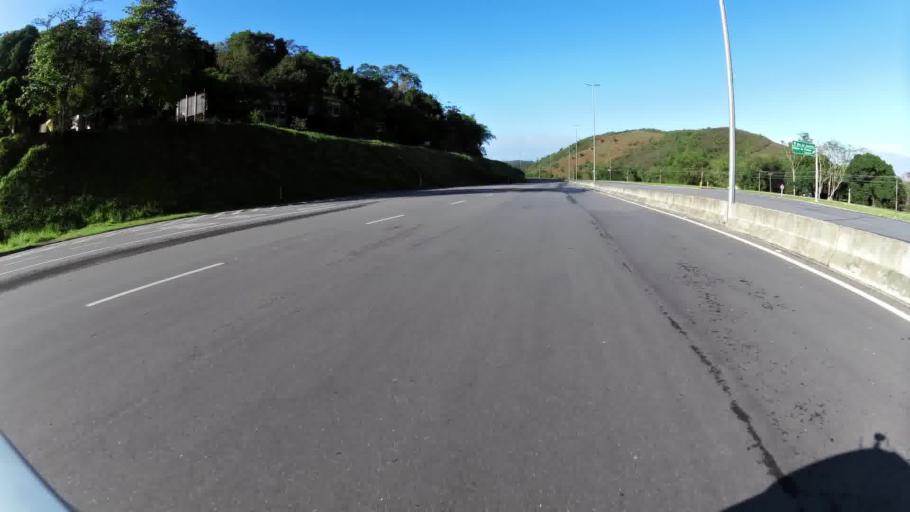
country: BR
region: Rio de Janeiro
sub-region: Petropolis
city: Petropolis
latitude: -22.6116
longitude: -43.2858
